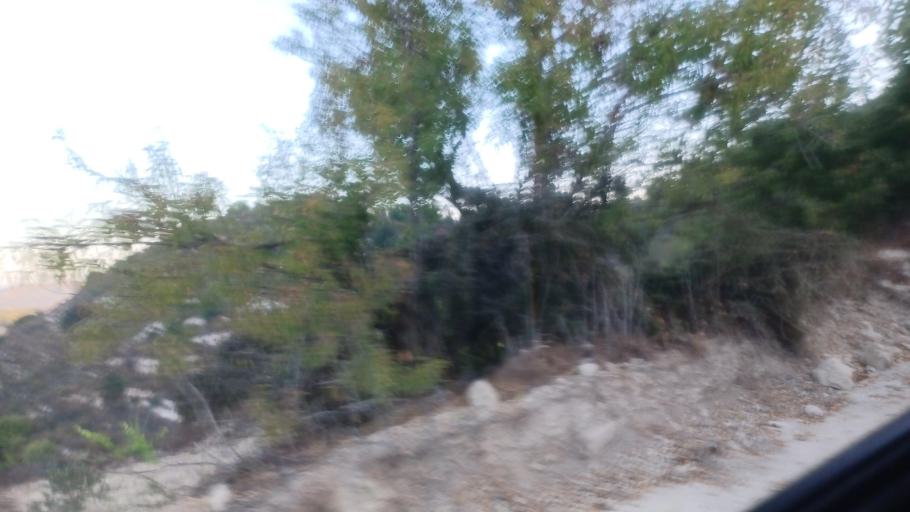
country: CY
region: Pafos
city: Tala
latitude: 34.8580
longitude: 32.4688
